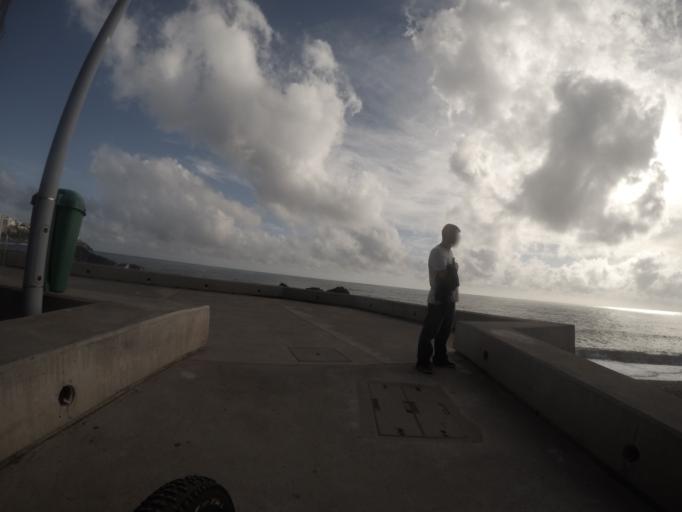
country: PT
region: Madeira
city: Camara de Lobos
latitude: 32.6424
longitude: -16.9582
